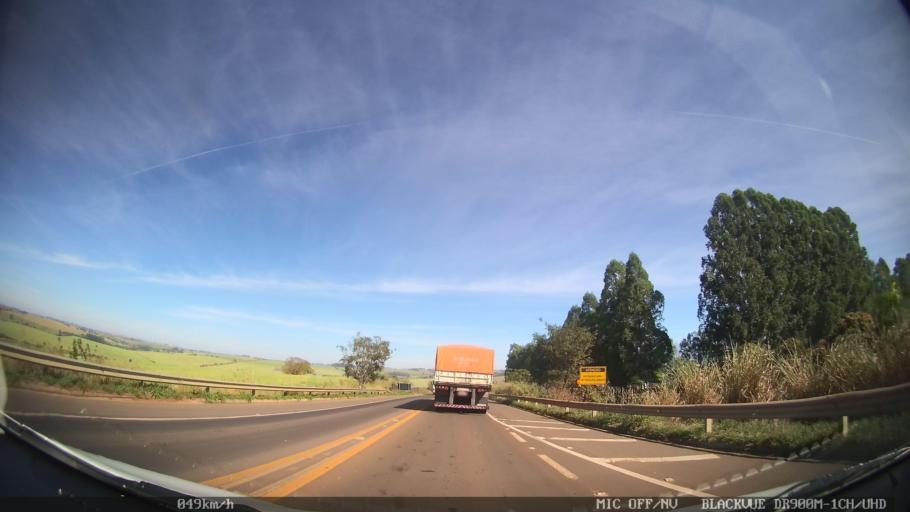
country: BR
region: Sao Paulo
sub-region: Pirassununga
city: Pirassununga
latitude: -22.0398
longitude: -47.4349
